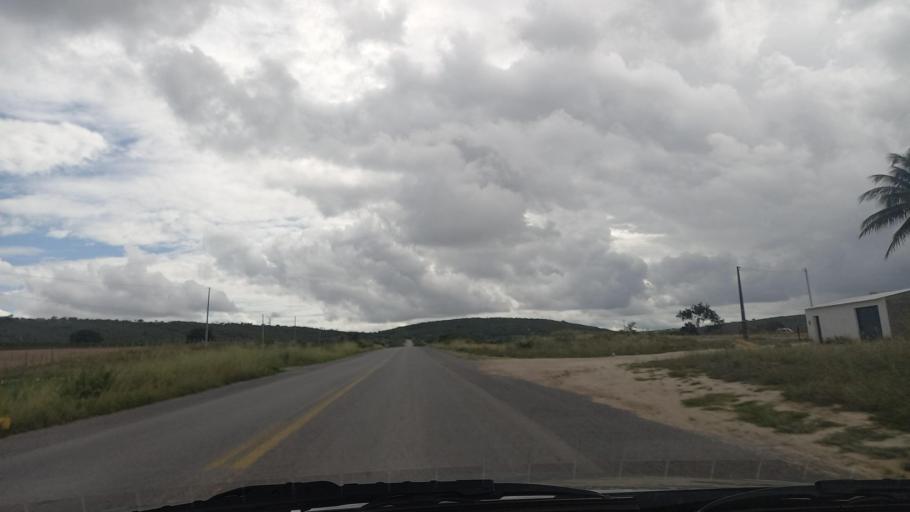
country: BR
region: Pernambuco
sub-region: Lajedo
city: Lajedo
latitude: -8.6710
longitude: -36.3860
